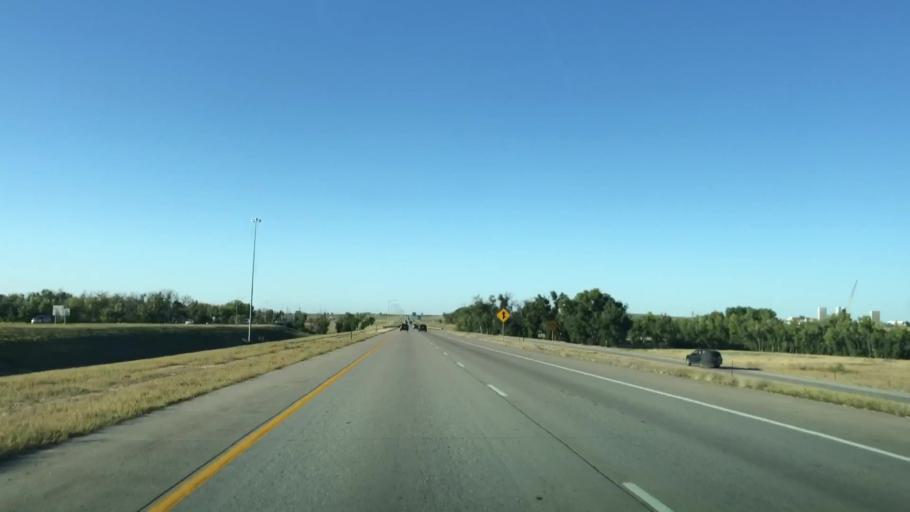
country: US
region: Colorado
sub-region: Adams County
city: Aurora
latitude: 39.7999
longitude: -104.7863
